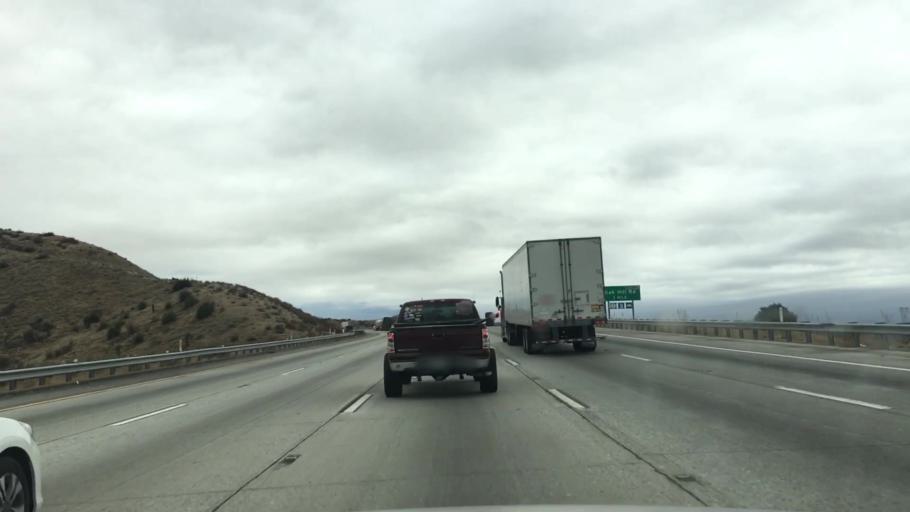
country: US
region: California
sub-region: San Bernardino County
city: Oak Hills
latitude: 34.3447
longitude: -117.4467
